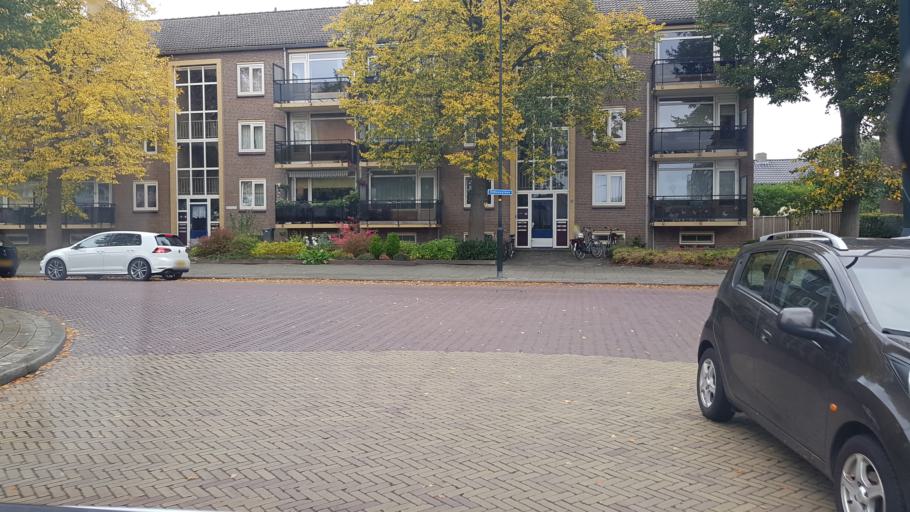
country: NL
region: Gelderland
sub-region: Gemeente Apeldoorn
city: Apeldoorn
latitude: 52.1902
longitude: 5.9674
